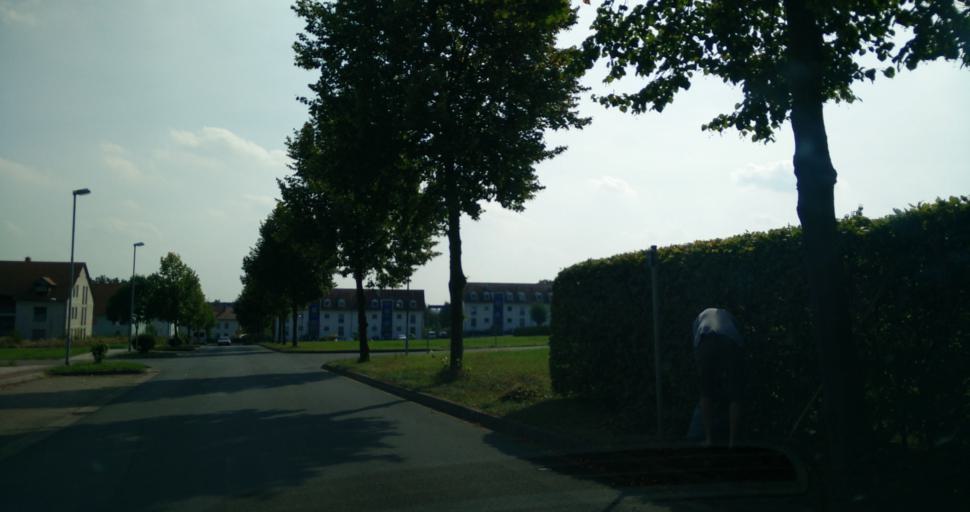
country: DE
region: Saxony
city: Colditz
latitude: 51.1330
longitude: 12.7910
